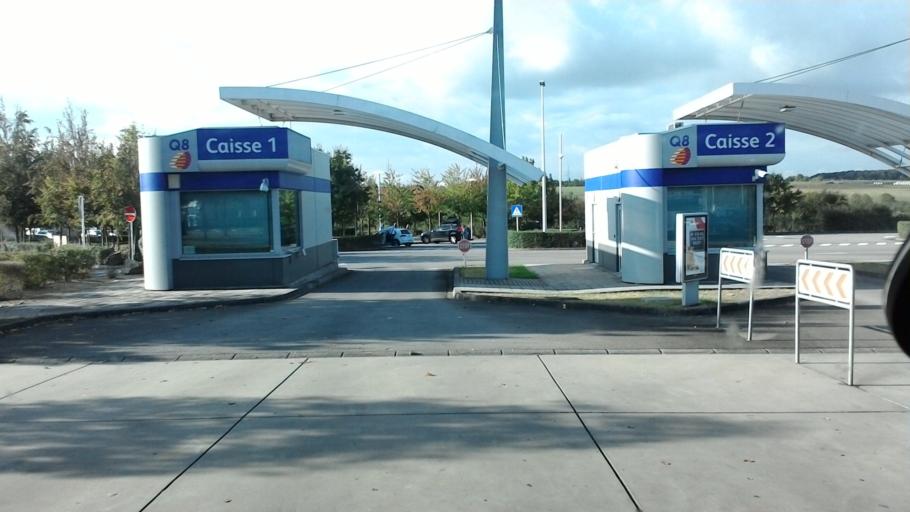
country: LU
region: Luxembourg
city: Capellen
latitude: 49.6370
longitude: 5.9715
